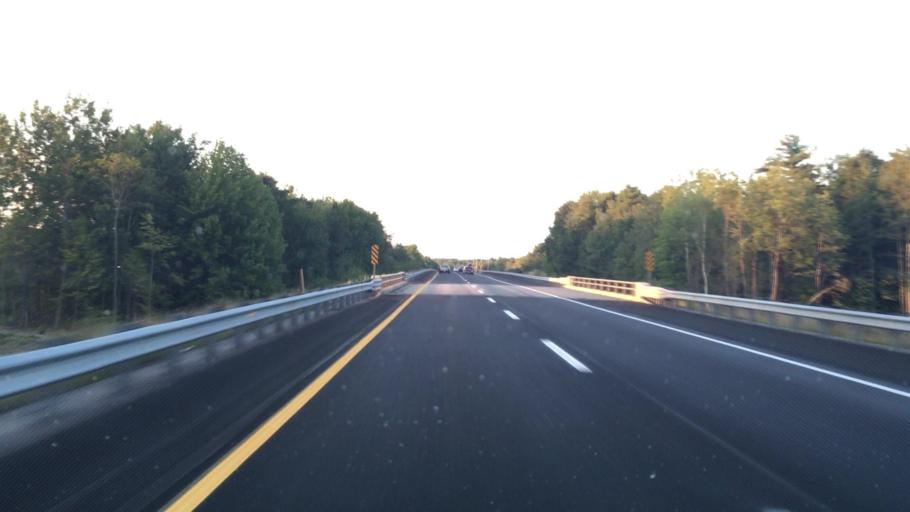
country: US
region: Maine
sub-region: Sagadahoc County
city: Topsham
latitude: 44.0167
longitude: -69.9197
